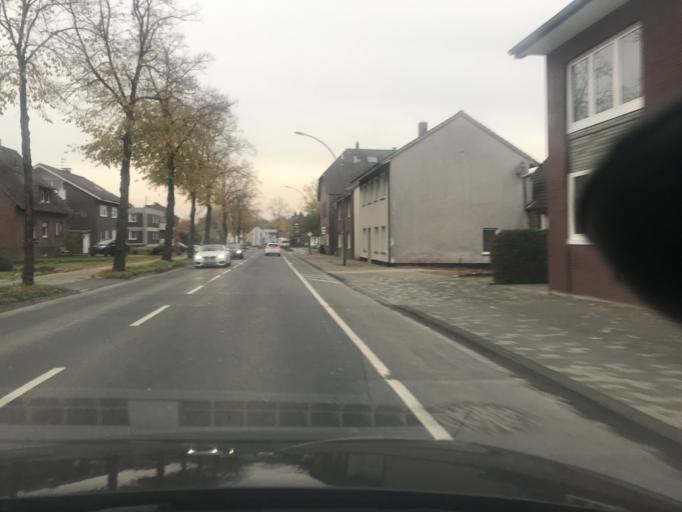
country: DE
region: North Rhine-Westphalia
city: Oelde
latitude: 51.8148
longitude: 8.1374
